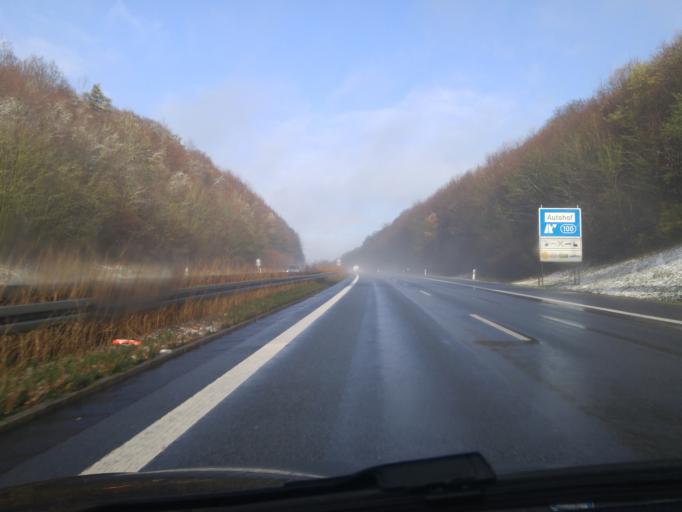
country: DE
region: Bavaria
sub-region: Regierungsbezirk Unterfranken
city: Unterpleichfeld
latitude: 49.8931
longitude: 10.0011
